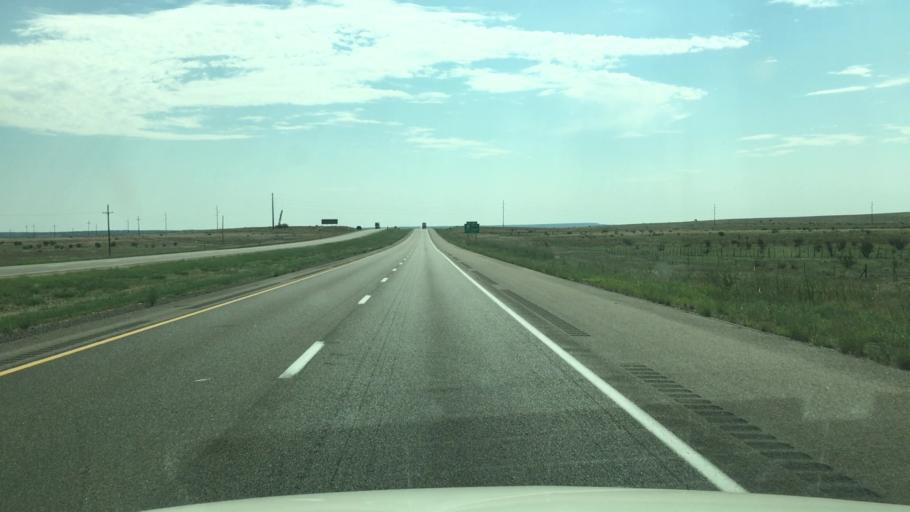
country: US
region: New Mexico
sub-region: Guadalupe County
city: Santa Rosa
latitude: 34.9784
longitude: -105.0318
